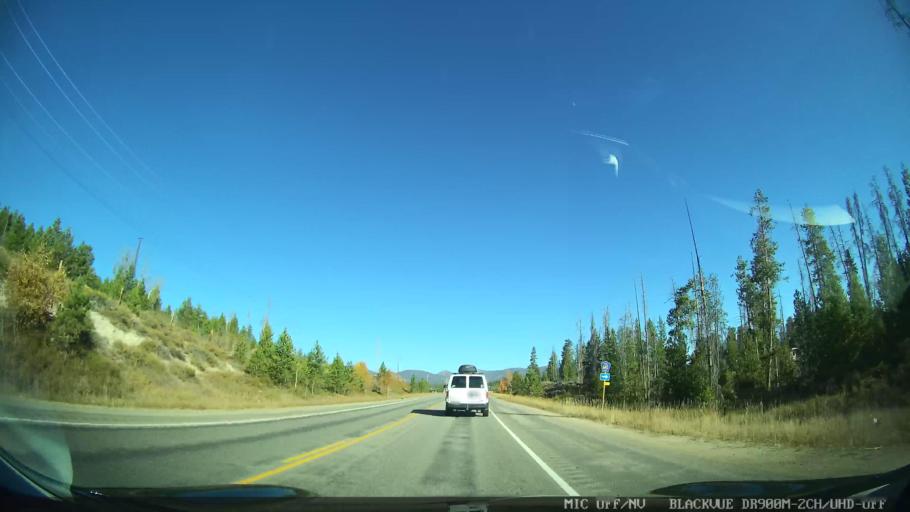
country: US
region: Colorado
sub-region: Grand County
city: Granby
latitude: 40.1687
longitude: -105.8996
